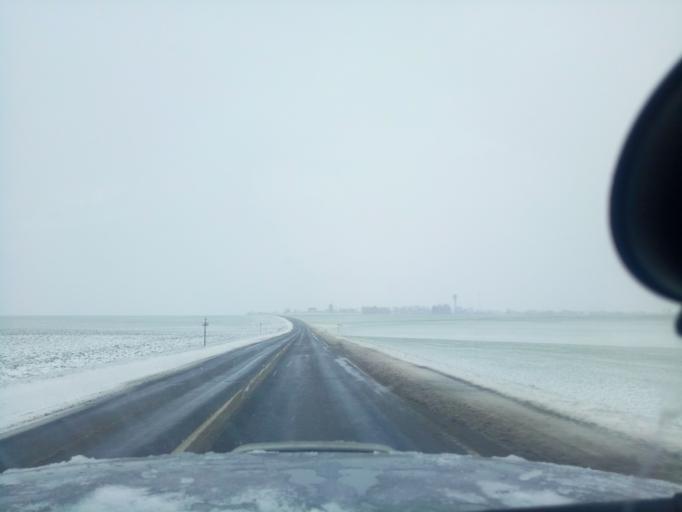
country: BY
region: Minsk
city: Haradzyeya
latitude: 53.3265
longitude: 26.5520
